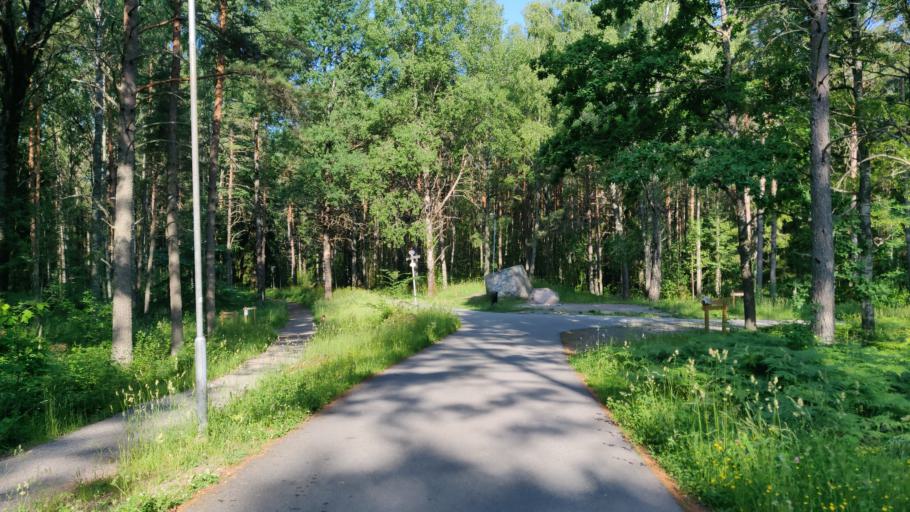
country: SE
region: OErebro
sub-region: Orebro Kommun
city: Orebro
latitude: 59.2856
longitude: 15.1649
